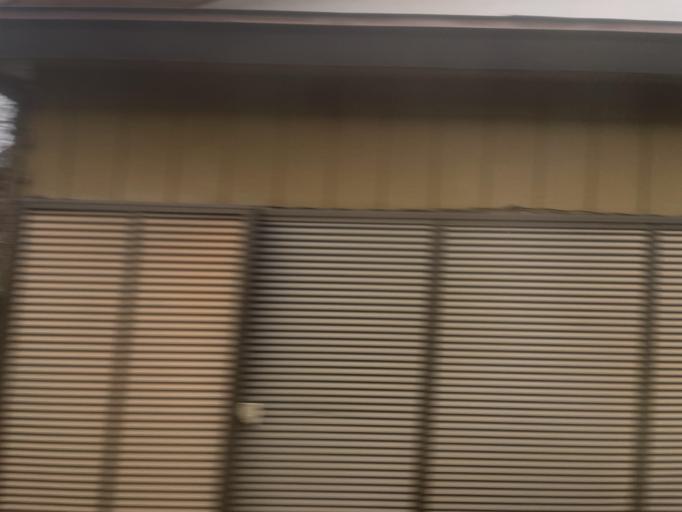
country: JP
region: Saitama
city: Kodamacho-kodamaminami
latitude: 36.1056
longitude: 139.1104
